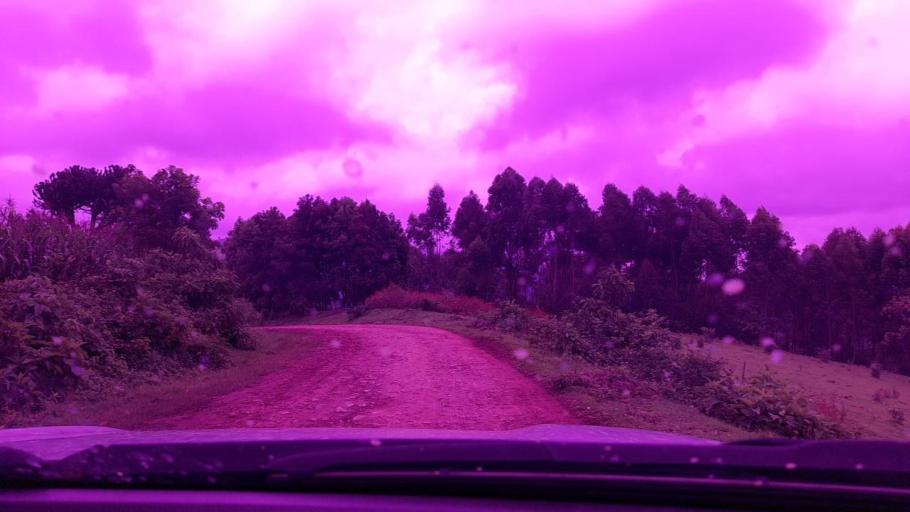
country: ET
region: Southern Nations, Nationalities, and People's Region
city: Bonga
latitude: 7.5503
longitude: 35.8440
